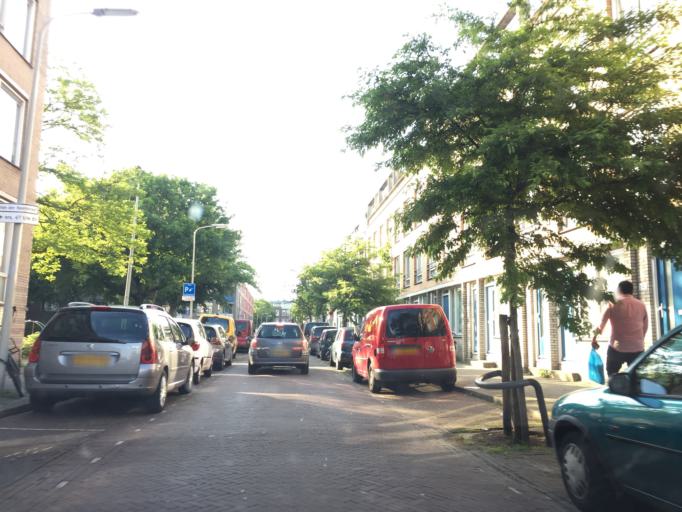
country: NL
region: South Holland
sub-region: Gemeente Den Haag
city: The Hague
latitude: 52.0686
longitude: 4.3006
